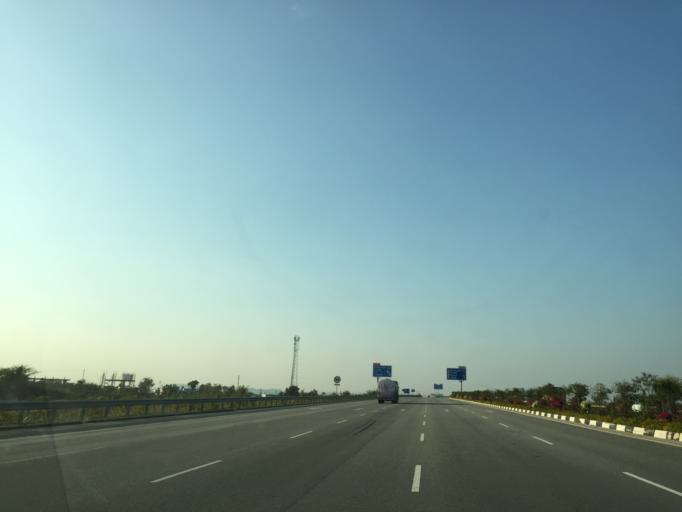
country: IN
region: Telangana
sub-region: Rangareddi
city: Ghatkesar
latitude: 17.5090
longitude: 78.6518
